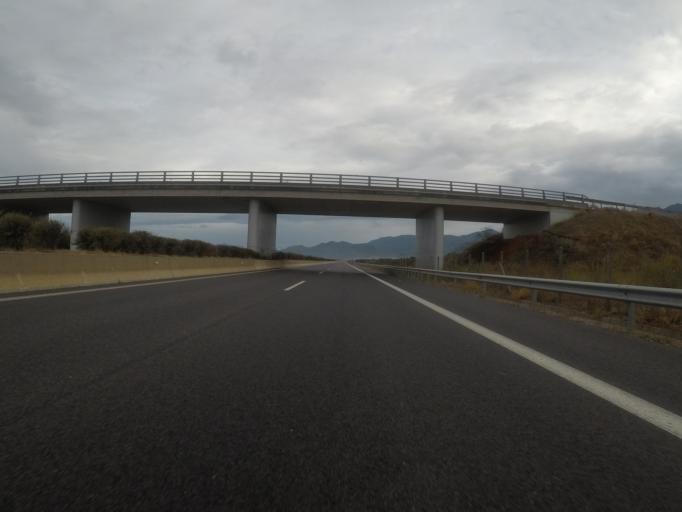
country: GR
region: Peloponnese
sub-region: Nomos Messinias
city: Thouria
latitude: 37.1021
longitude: 22.0337
